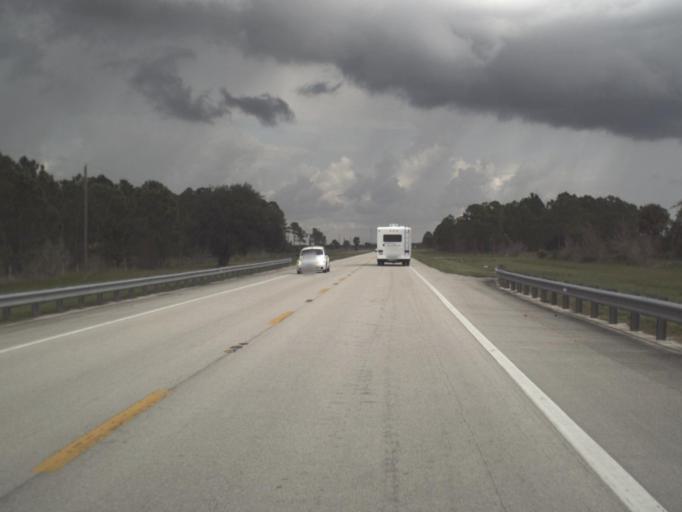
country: US
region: Florida
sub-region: Hendry County
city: Port LaBelle
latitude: 26.8914
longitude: -81.3446
